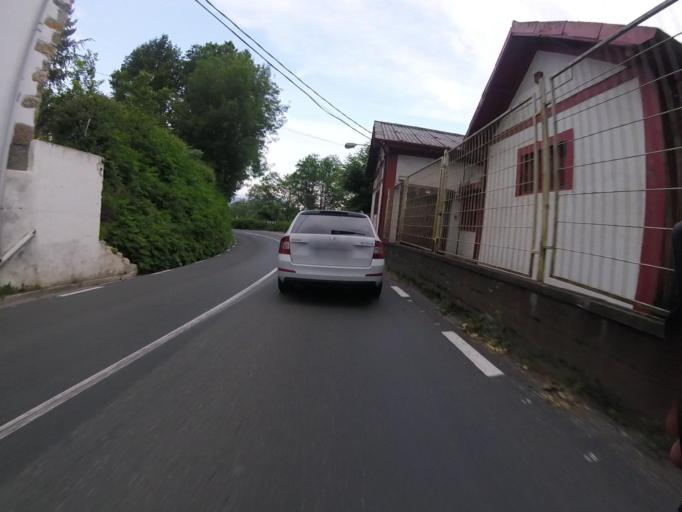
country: ES
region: Basque Country
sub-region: Provincia de Guipuzcoa
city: Errenteria
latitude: 43.2886
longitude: -1.9074
